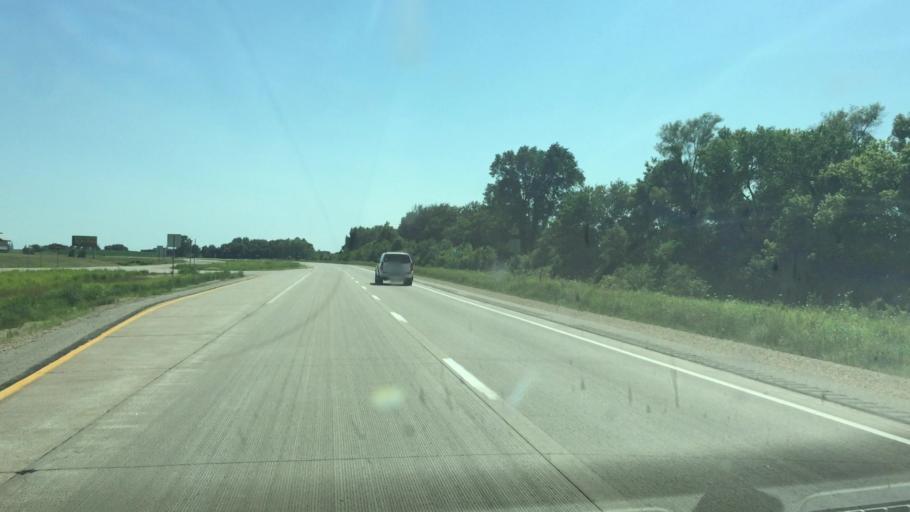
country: US
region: Iowa
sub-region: Jones County
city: Monticello
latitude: 42.2001
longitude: -91.2089
